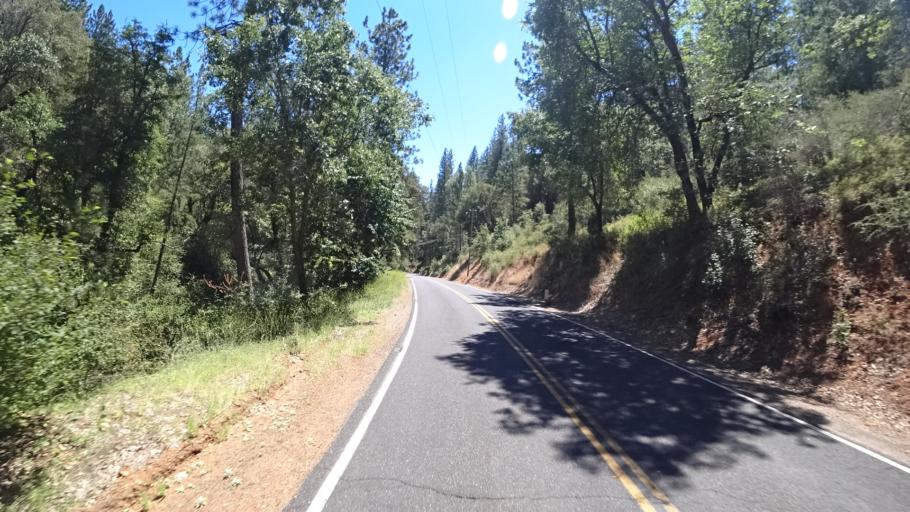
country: US
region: California
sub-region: Calaveras County
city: Mountain Ranch
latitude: 38.2994
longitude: -120.5037
